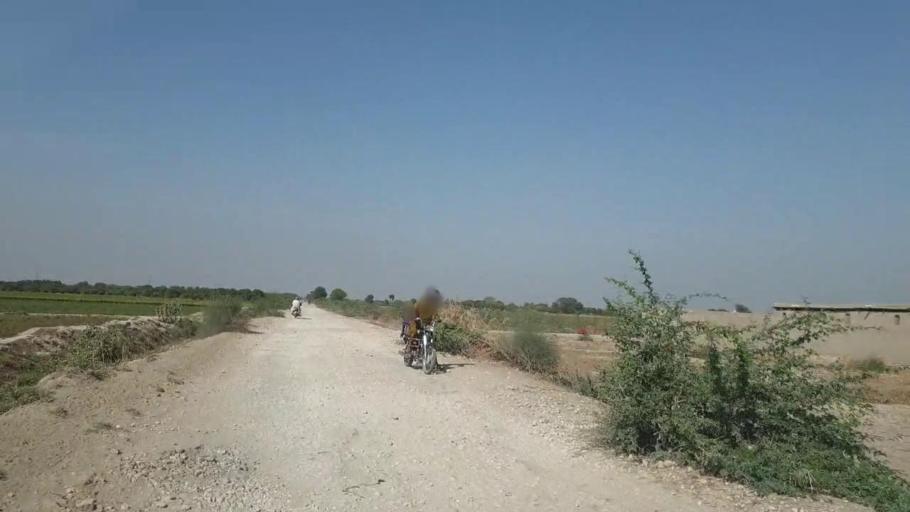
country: PK
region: Sindh
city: Nabisar
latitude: 25.0202
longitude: 69.5245
